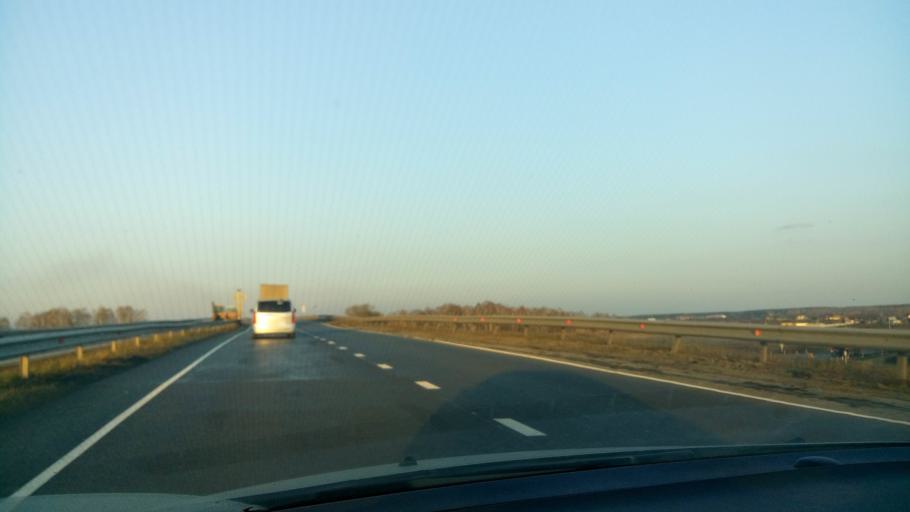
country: RU
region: Sverdlovsk
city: Yelanskiy
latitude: 56.8095
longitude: 62.5278
